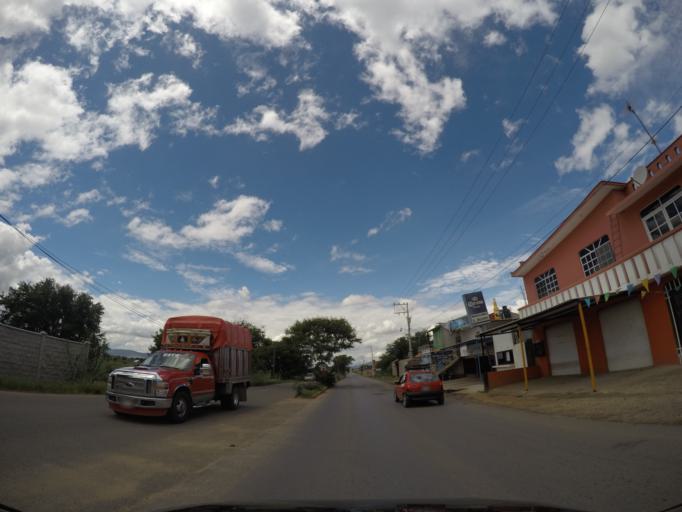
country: MX
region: Oaxaca
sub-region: Santa Cruz Xoxocotlan
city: San Isidro Monjas
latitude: 16.9953
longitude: -96.7425
